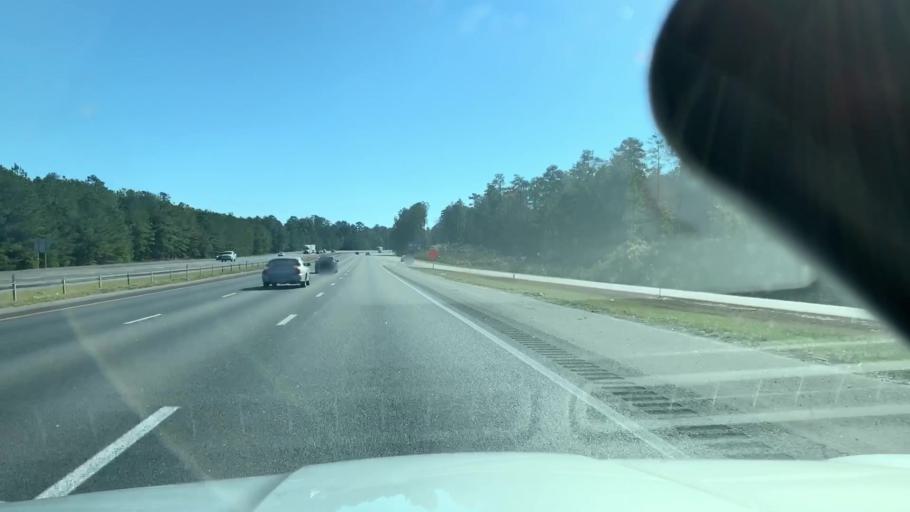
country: US
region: South Carolina
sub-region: Richland County
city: Forest Acres
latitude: 33.9939
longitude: -80.9576
